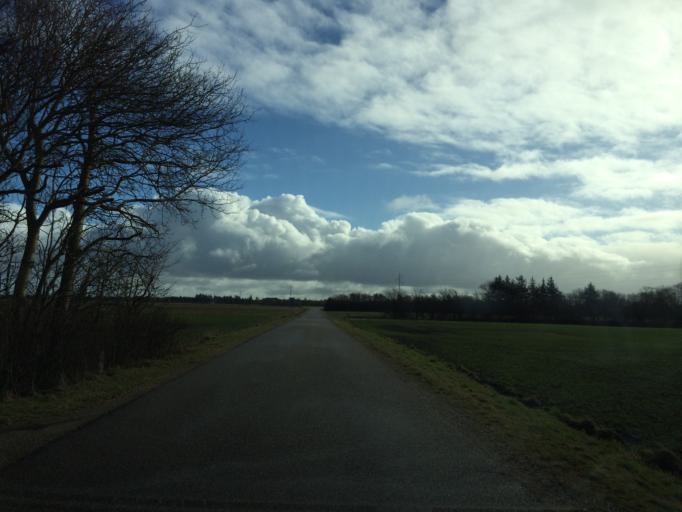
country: DK
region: Central Jutland
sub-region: Holstebro Kommune
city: Ulfborg
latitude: 56.2824
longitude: 8.3309
